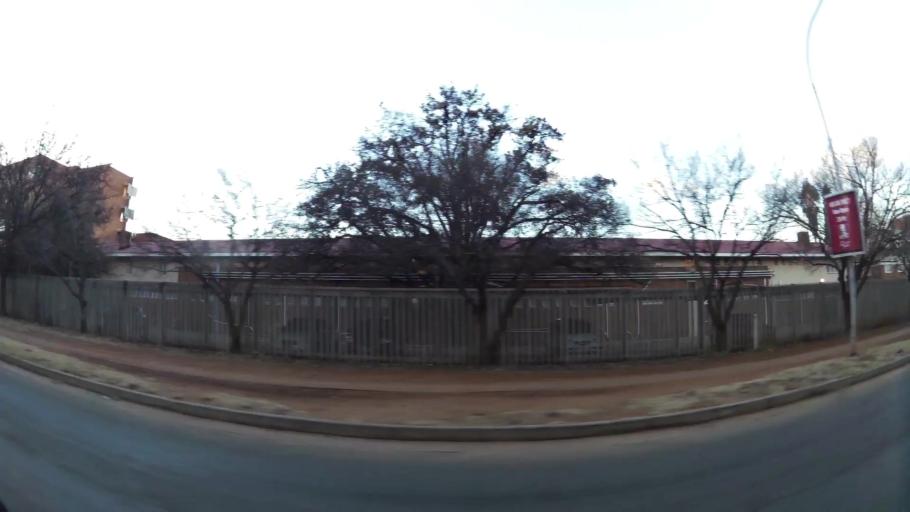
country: ZA
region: North-West
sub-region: Dr Kenneth Kaunda District Municipality
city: Potchefstroom
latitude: -26.6911
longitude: 27.0918
